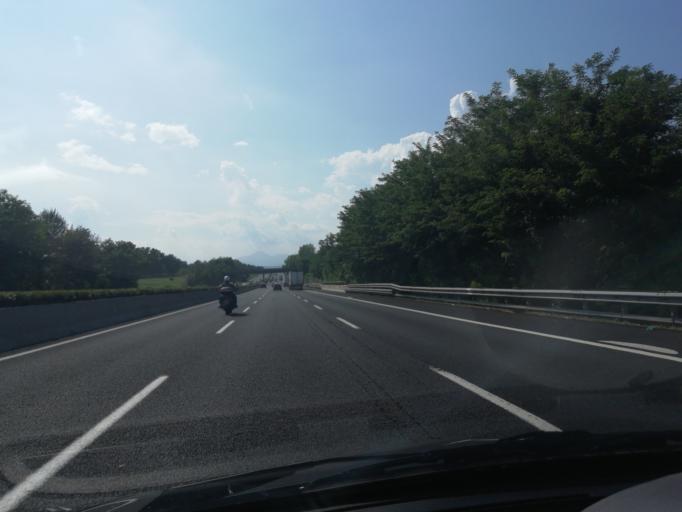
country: IT
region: Latium
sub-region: Provincia di Frosinone
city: Pofi
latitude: 41.5511
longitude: 13.4519
